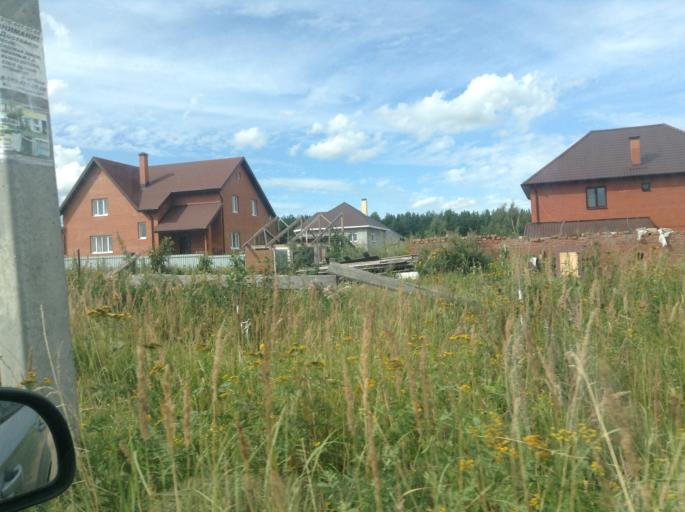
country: RU
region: Moskovskaya
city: Yegor'yevsk
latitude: 55.3656
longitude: 39.0944
